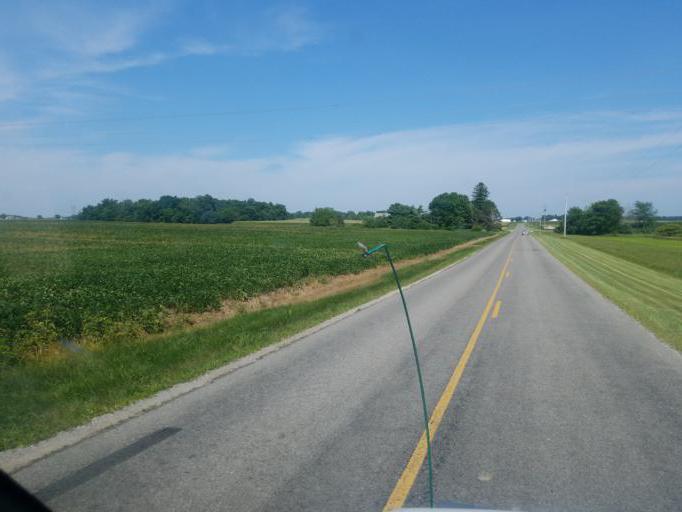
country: US
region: Ohio
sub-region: Shelby County
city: Botkins
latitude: 40.4975
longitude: -84.1167
